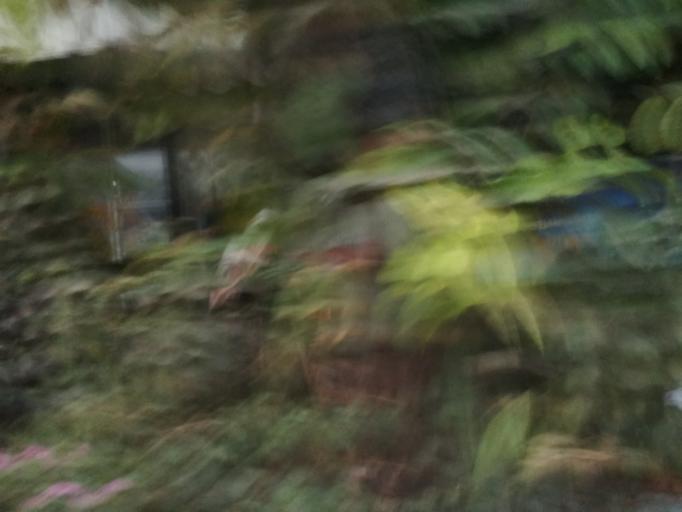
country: ID
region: West Java
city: Caringin
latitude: -6.7165
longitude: 106.8202
